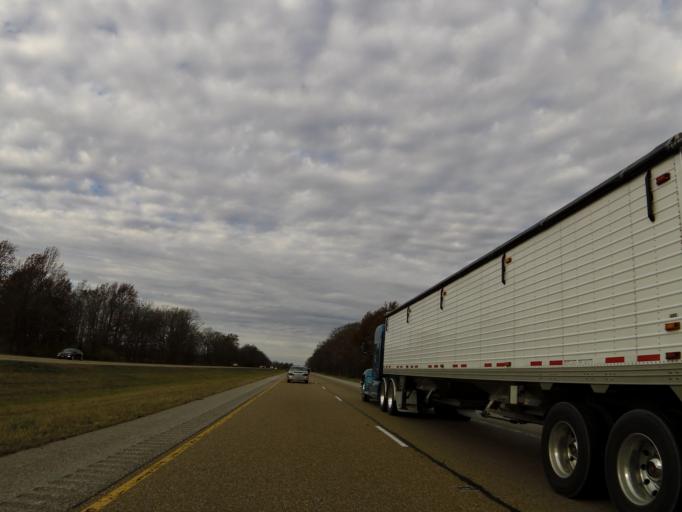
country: US
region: Illinois
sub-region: Clinton County
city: Wamac
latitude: 38.3876
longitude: -89.1480
